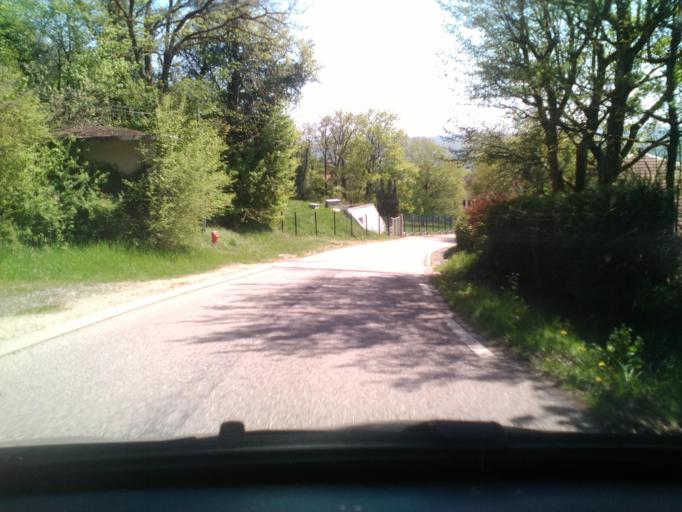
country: FR
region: Lorraine
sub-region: Departement de Meurthe-et-Moselle
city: Ludres
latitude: 48.6274
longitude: 6.1606
